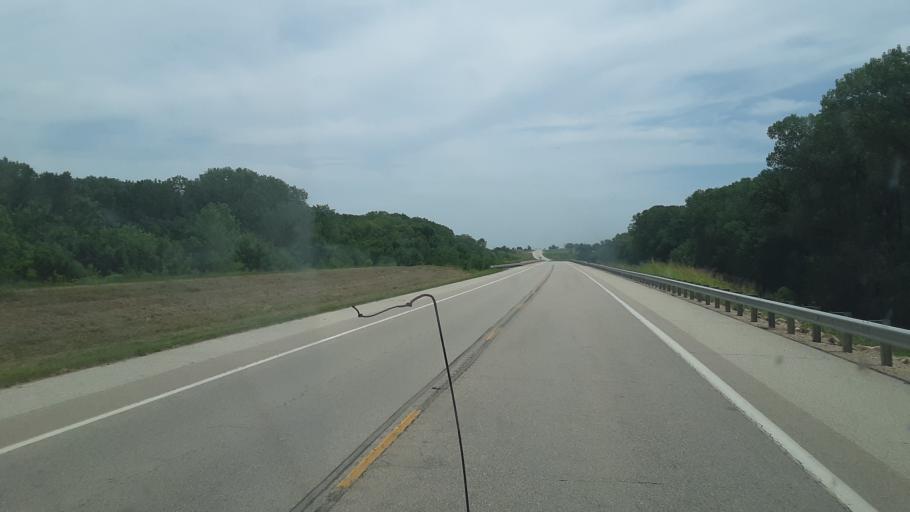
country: US
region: Kansas
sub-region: Woodson County
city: Yates Center
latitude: 37.8362
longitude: -95.9670
